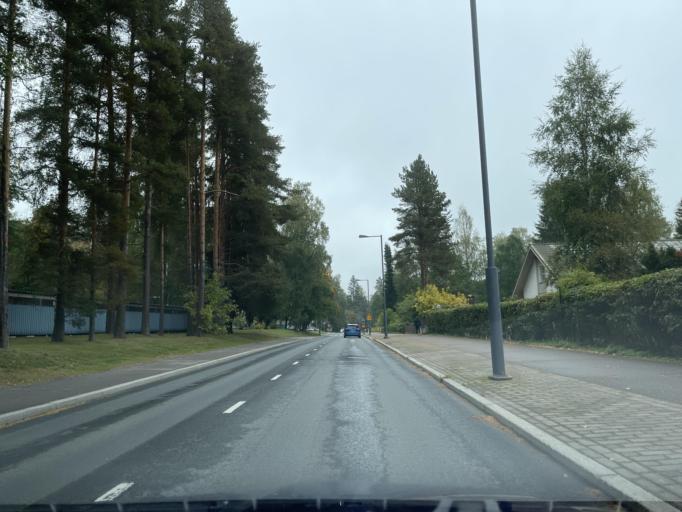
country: FI
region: Uusimaa
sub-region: Helsinki
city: Hyvinge
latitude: 60.6241
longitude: 24.8563
